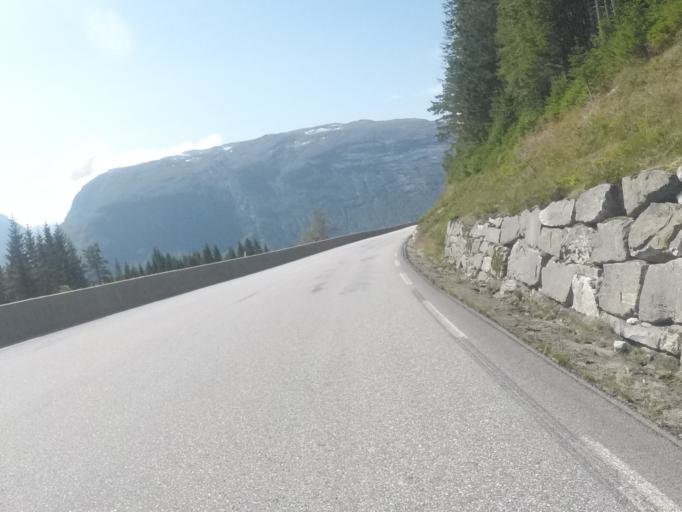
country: NO
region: Sogn og Fjordane
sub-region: Jolster
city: Skei
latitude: 61.7589
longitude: 6.5000
